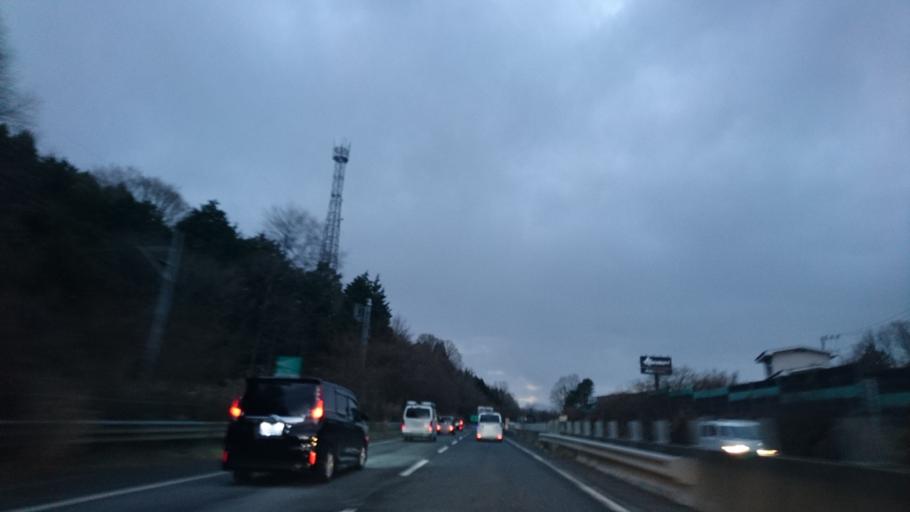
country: JP
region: Nara
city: Haibara-akanedai
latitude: 34.6235
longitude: 135.9833
